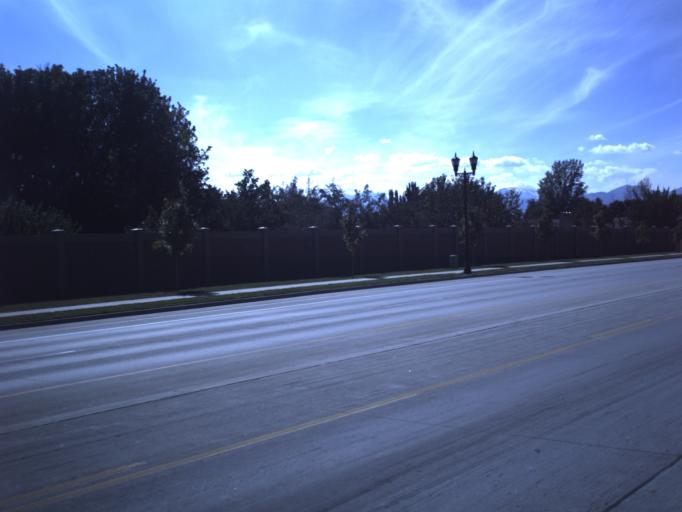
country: US
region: Utah
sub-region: Salt Lake County
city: South Jordan Heights
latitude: 40.5623
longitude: -111.9507
